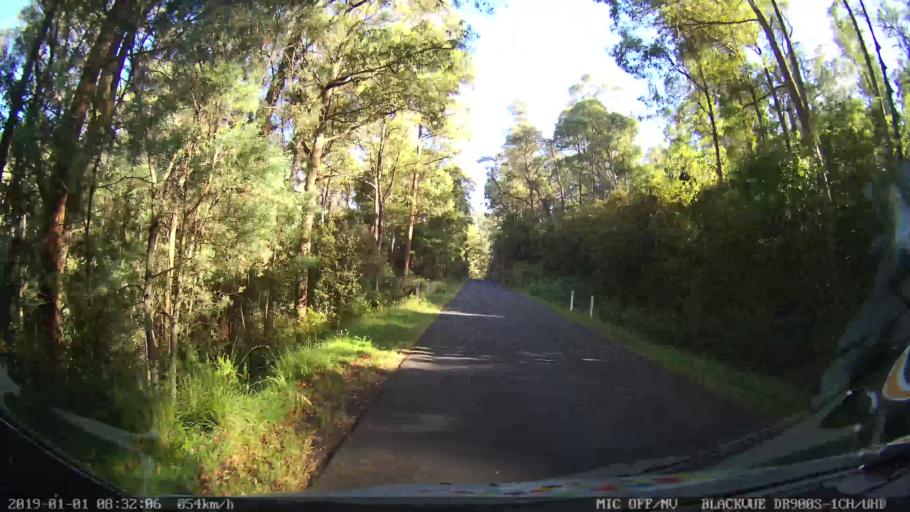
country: AU
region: New South Wales
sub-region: Snowy River
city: Jindabyne
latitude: -36.3647
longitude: 148.2057
